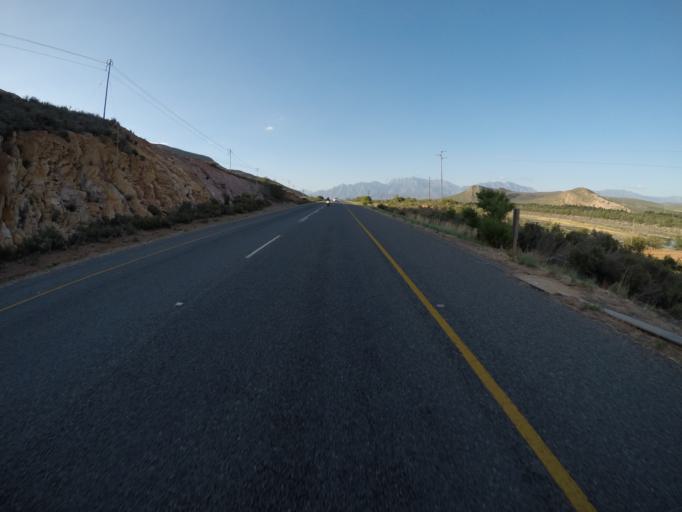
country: ZA
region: Western Cape
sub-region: Cape Winelands District Municipality
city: Worcester
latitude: -33.7448
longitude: 19.4827
